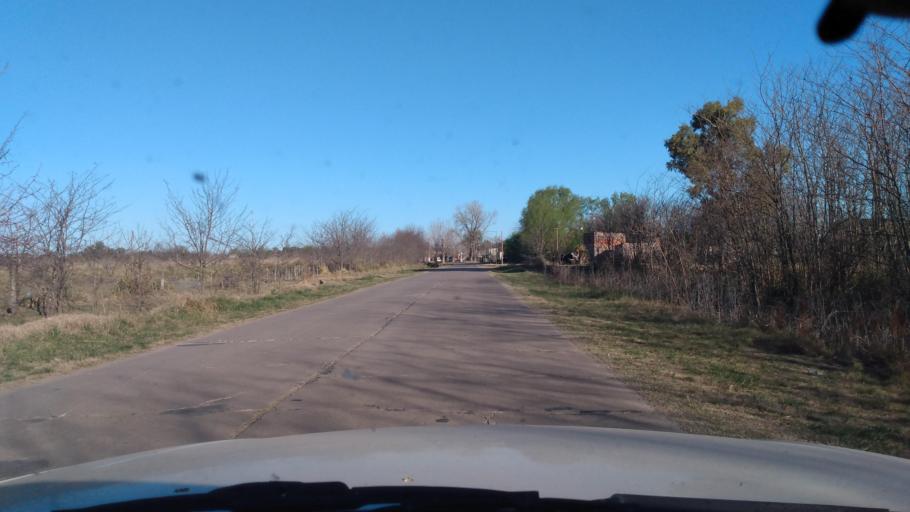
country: AR
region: Buenos Aires
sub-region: Partido de Lujan
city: Lujan
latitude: -34.6191
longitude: -59.2581
